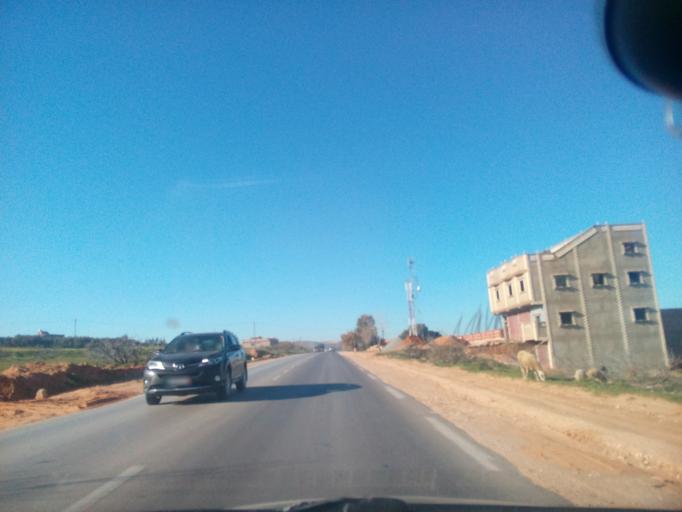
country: DZ
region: Relizane
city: Relizane
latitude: 35.9086
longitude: 0.5081
